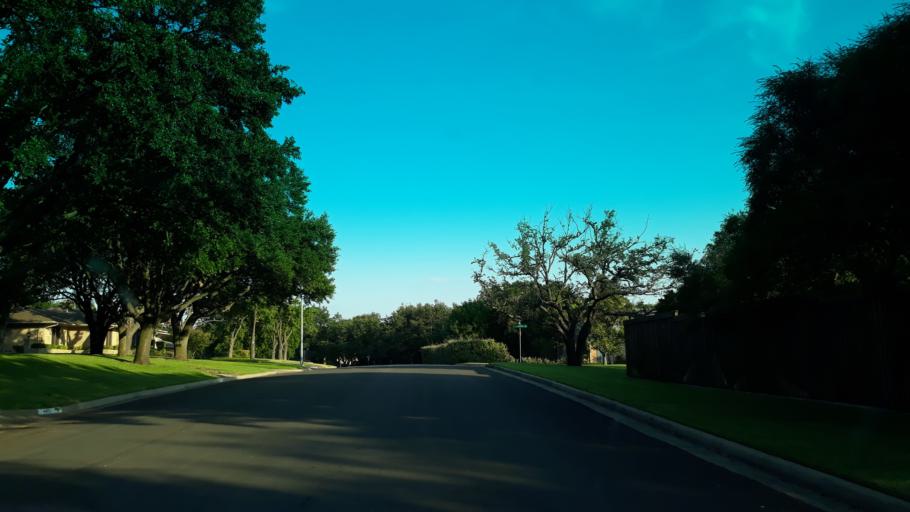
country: US
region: Texas
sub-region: Dallas County
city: Addison
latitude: 32.9436
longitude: -96.7901
